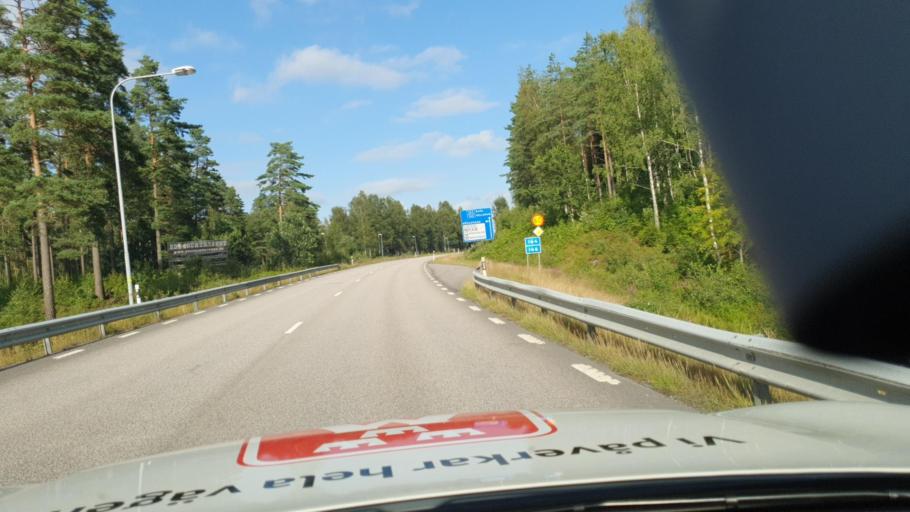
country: SE
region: Vaestra Goetaland
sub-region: Dals-Ed Kommun
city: Ed
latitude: 58.8995
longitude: 11.9379
